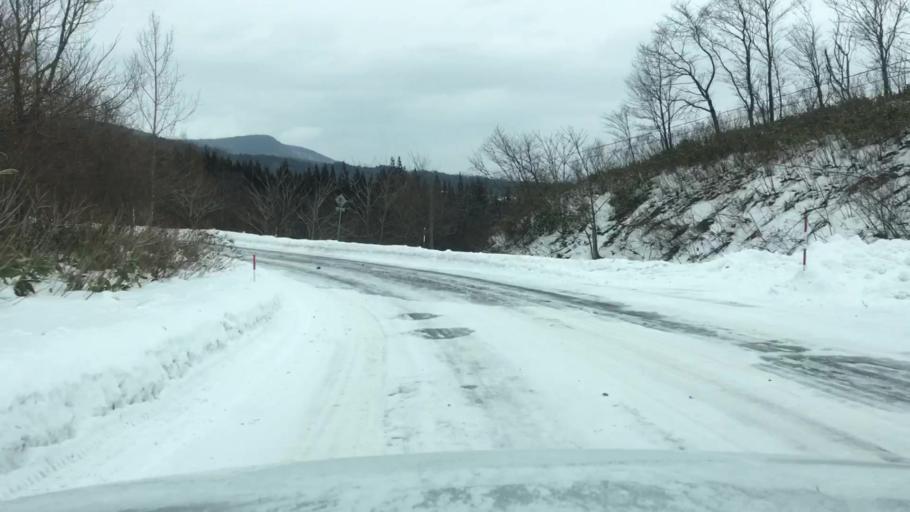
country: JP
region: Iwate
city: Shizukuishi
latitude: 39.9361
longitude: 141.0021
